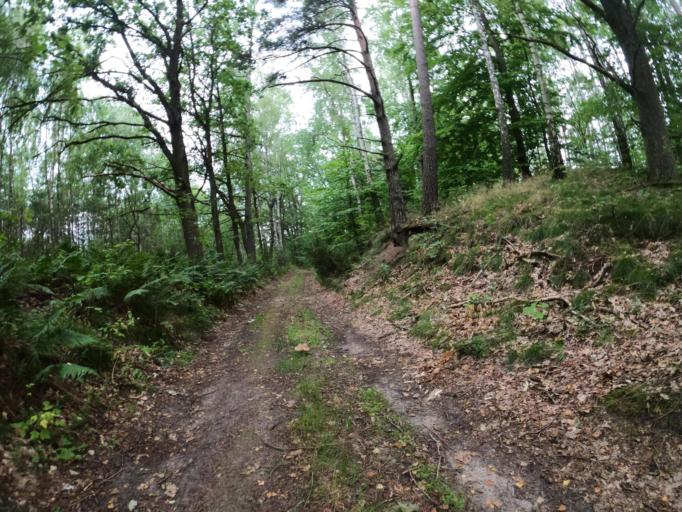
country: PL
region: West Pomeranian Voivodeship
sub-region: Powiat szczecinecki
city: Grzmiaca
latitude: 53.7554
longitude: 16.5020
